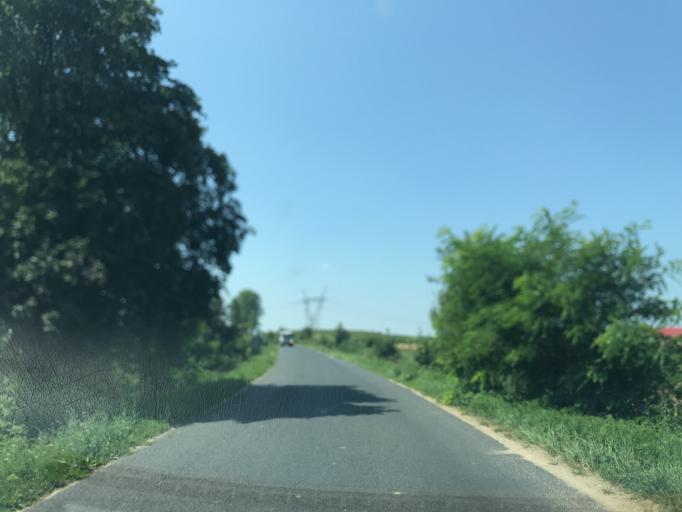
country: PL
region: Kujawsko-Pomorskie
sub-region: Powiat lipnowski
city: Chrostkowo
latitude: 52.9963
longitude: 19.2325
